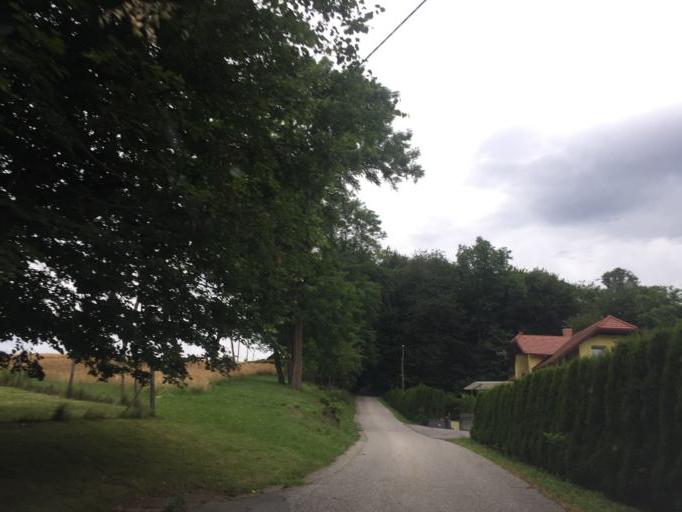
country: SI
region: Gornja Radgona
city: Gornja Radgona
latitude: 46.6731
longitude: 15.9682
